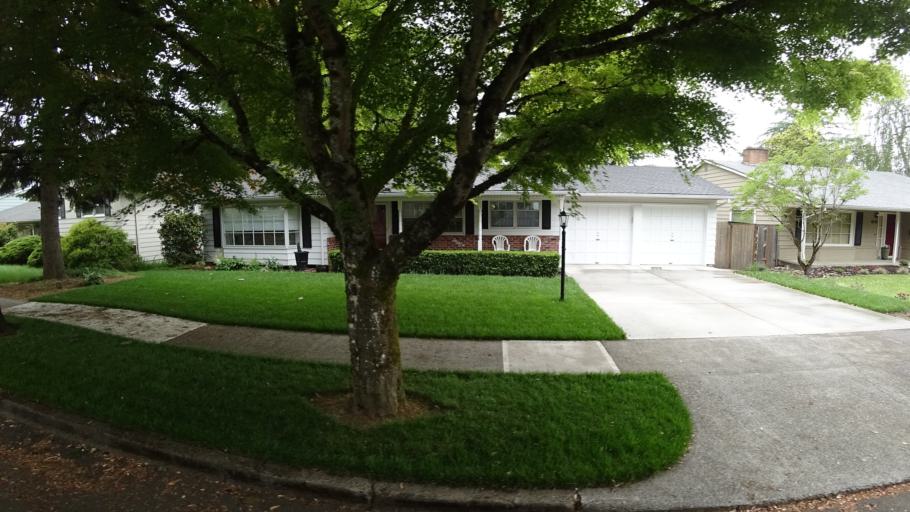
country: US
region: Oregon
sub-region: Washington County
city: Raleigh Hills
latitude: 45.4806
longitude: -122.7737
